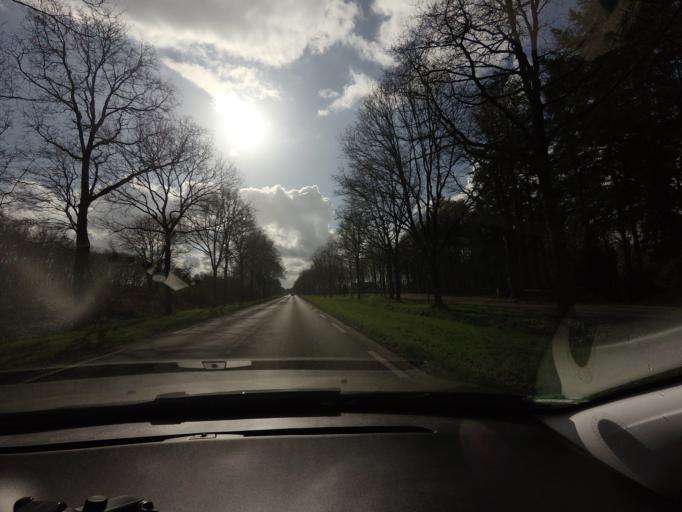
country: NL
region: Drenthe
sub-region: Gemeente Assen
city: Assen
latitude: 52.9117
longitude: 6.5413
